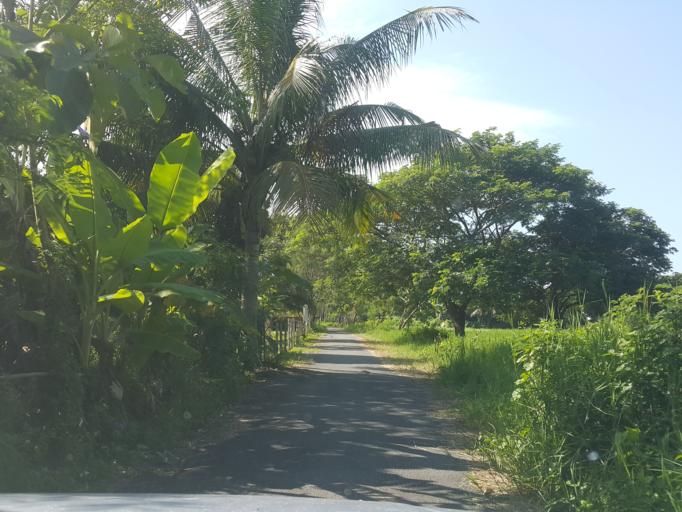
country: TH
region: Chiang Mai
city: Saraphi
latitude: 18.7317
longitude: 99.0435
